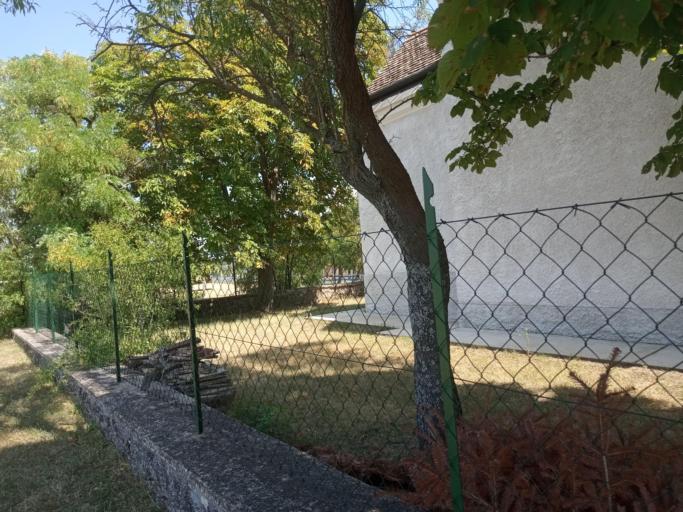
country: HU
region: Somogy
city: Balatonszarszo
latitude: 46.9070
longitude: 17.8055
